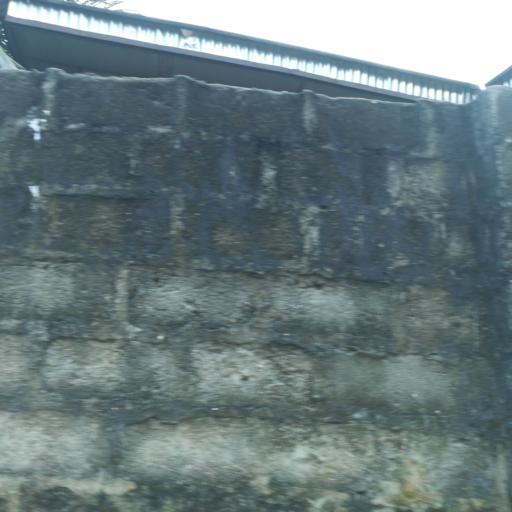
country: NG
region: Rivers
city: Okrika
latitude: 4.7781
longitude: 7.0606
